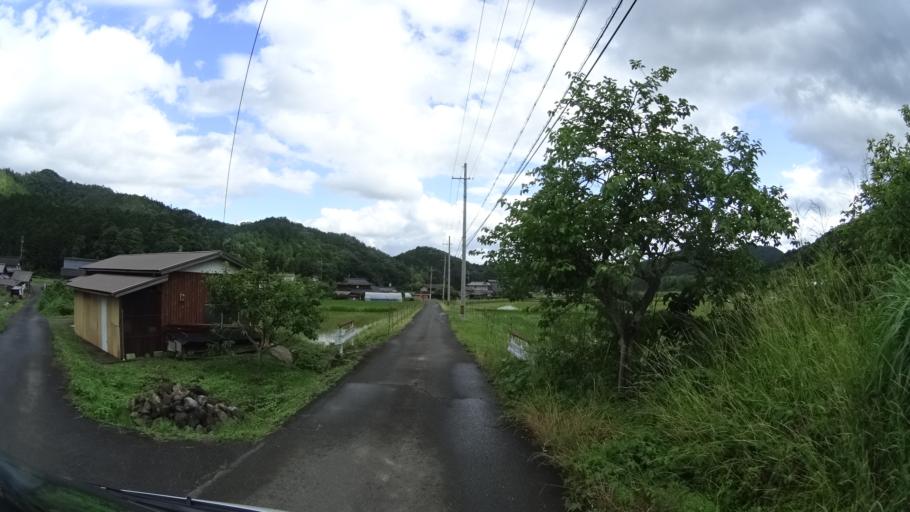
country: JP
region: Kyoto
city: Ayabe
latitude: 35.3836
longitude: 135.2393
